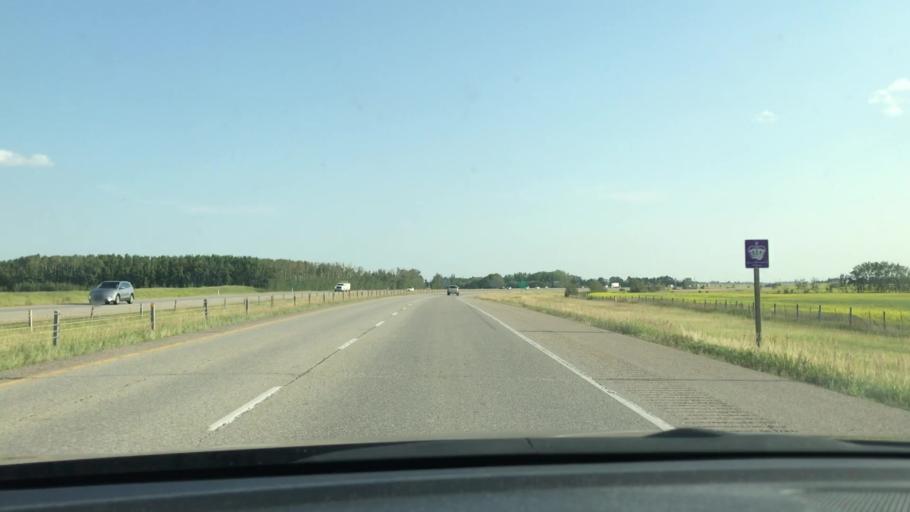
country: CA
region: Alberta
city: Leduc
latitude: 53.2466
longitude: -113.5619
